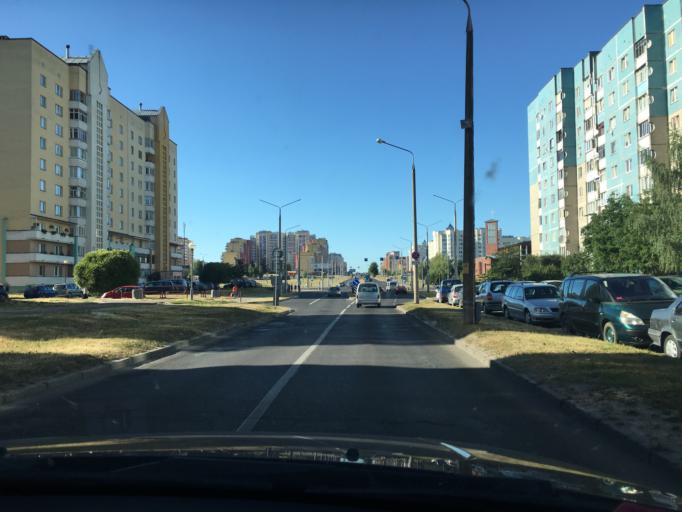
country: BY
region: Grodnenskaya
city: Hrodna
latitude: 53.7054
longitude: 23.8496
